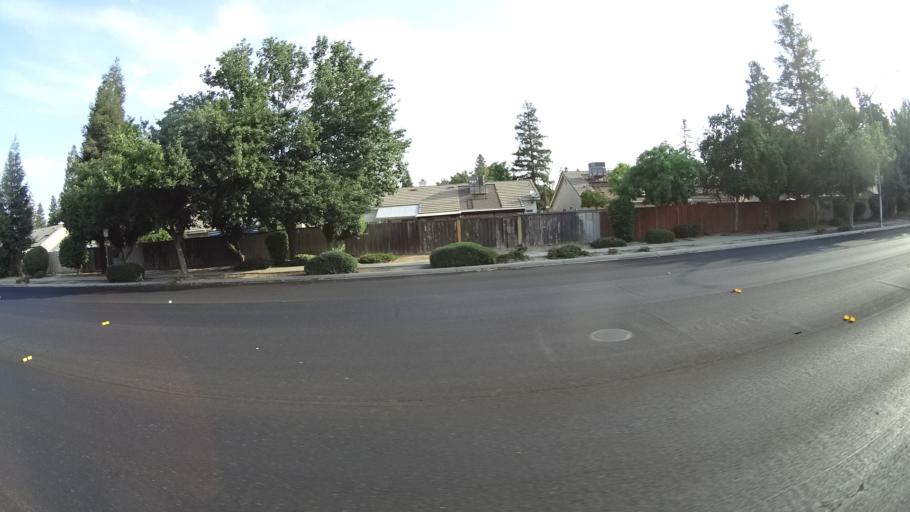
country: US
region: California
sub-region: Fresno County
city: West Park
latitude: 36.7719
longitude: -119.8671
